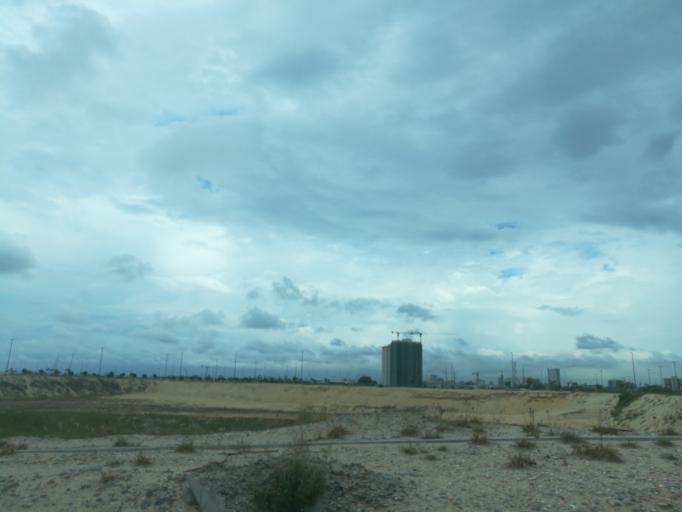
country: NG
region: Lagos
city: Ikoyi
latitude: 6.4139
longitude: 3.4159
